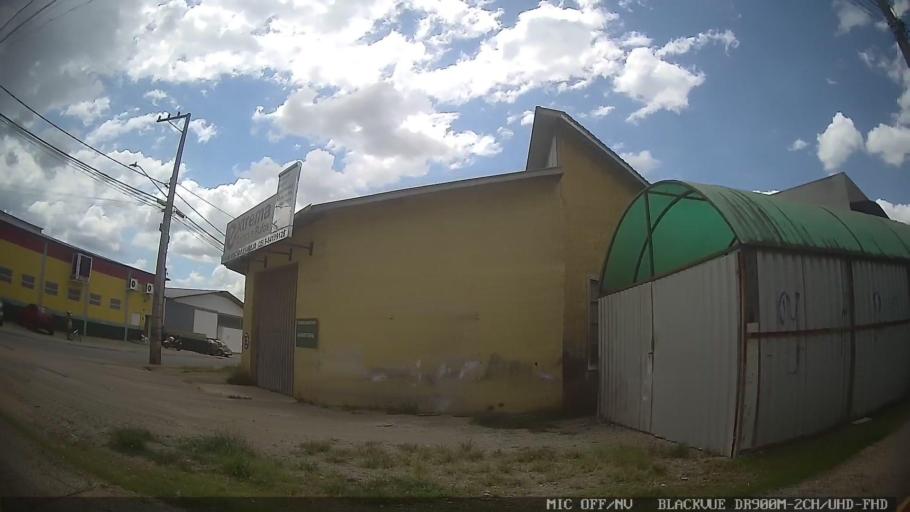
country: BR
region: Minas Gerais
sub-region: Extrema
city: Extrema
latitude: -22.8548
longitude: -46.3114
